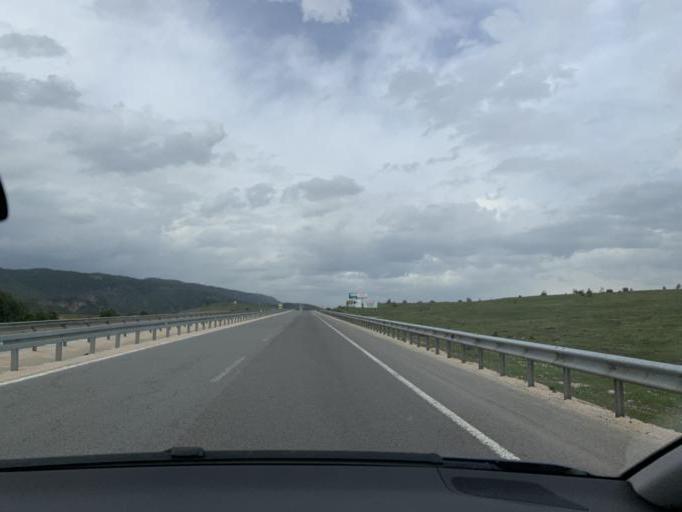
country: TR
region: Bolu
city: Gerede
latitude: 40.7936
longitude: 32.1456
